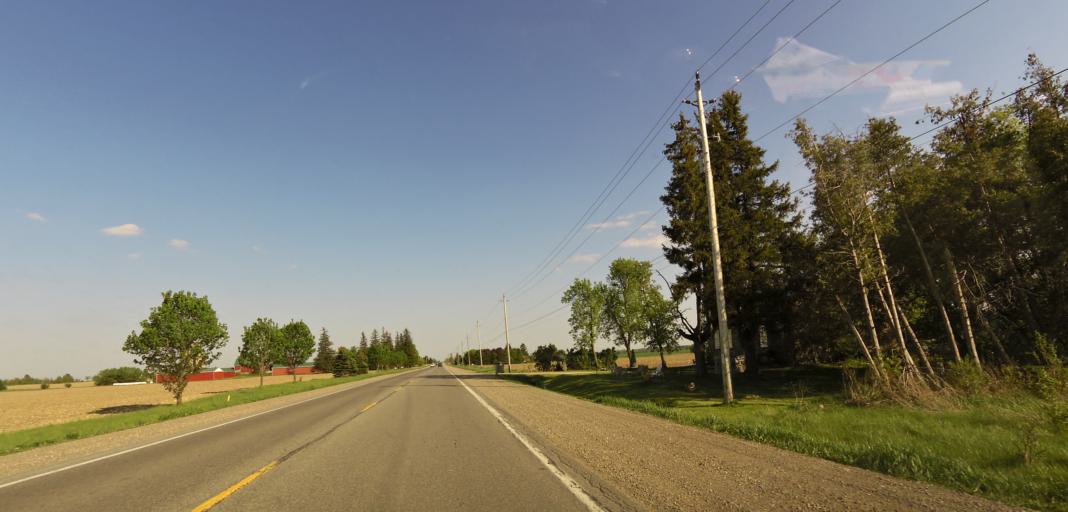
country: CA
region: Ontario
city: Brampton
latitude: 43.8488
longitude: -79.8383
